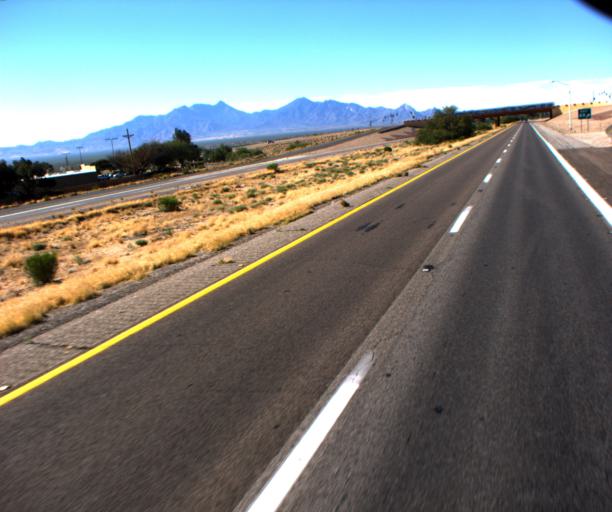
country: US
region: Arizona
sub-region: Pima County
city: Green Valley
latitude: 31.9097
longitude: -110.9859
